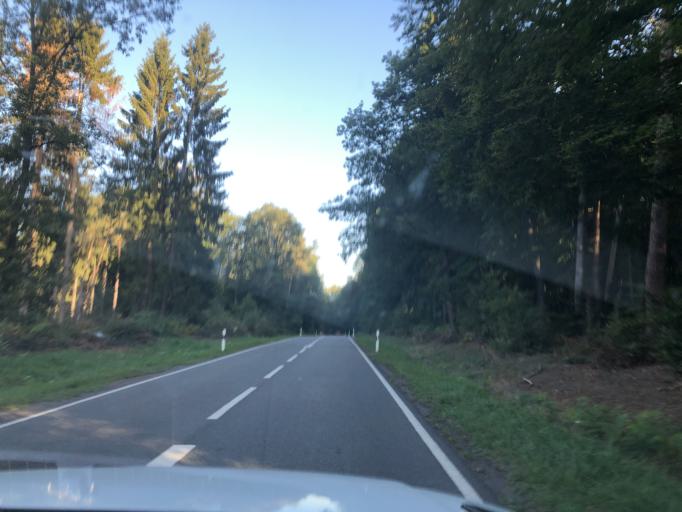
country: DE
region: Saarland
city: Puttlingen
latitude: 49.3223
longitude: 6.8662
